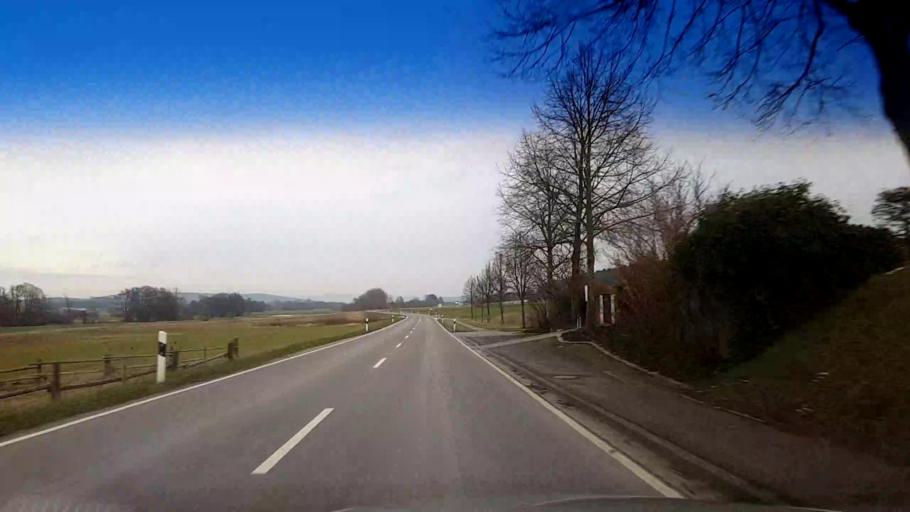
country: DE
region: Bavaria
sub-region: Upper Franconia
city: Pommersfelden
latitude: 49.8182
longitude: 10.8114
